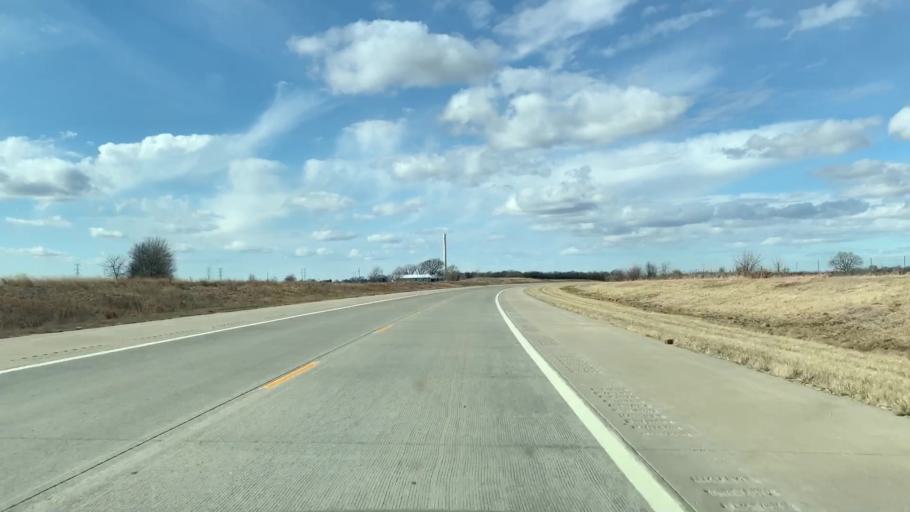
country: US
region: Kansas
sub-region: Labette County
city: Parsons
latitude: 37.3519
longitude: -95.2072
